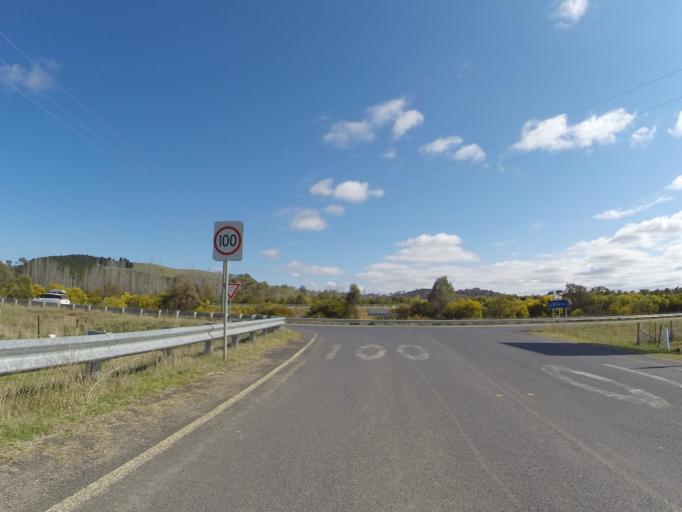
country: AU
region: Australian Capital Territory
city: Kaleen
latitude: -35.1955
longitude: 149.2208
